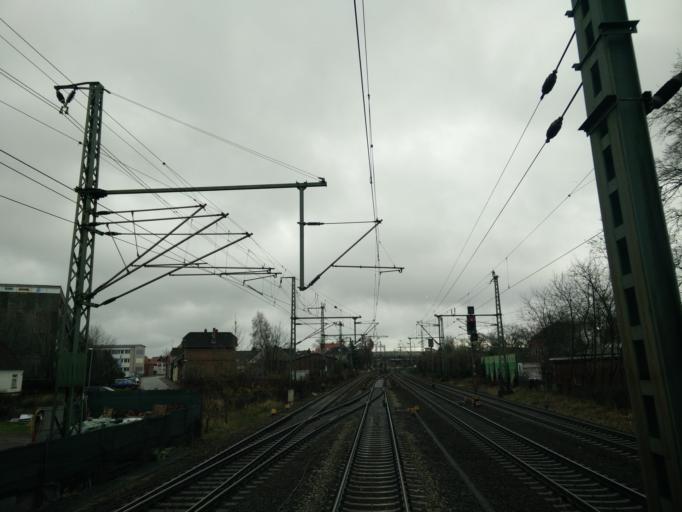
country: DE
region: Mecklenburg-Vorpommern
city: Ludwigslust
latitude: 53.3338
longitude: 11.4965
